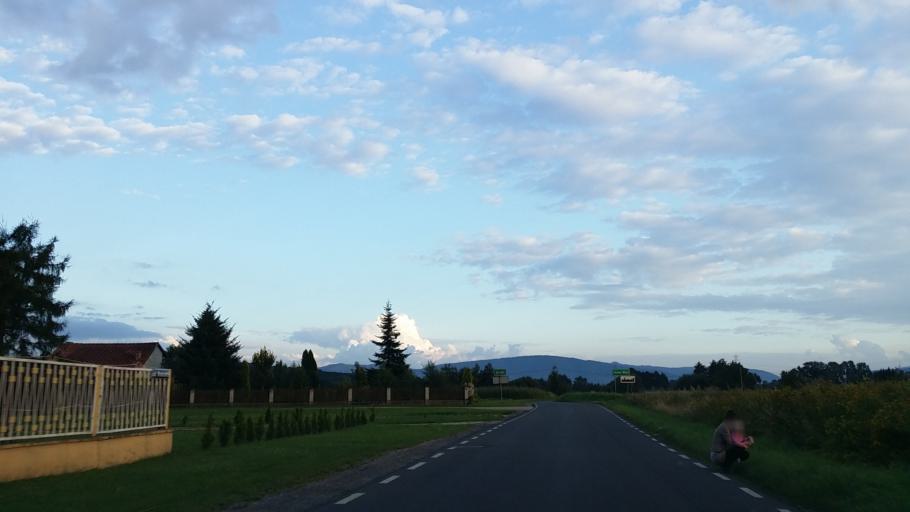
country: PL
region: Lesser Poland Voivodeship
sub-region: Powiat oswiecimski
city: Nowa Wies
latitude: 49.9108
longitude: 19.2291
